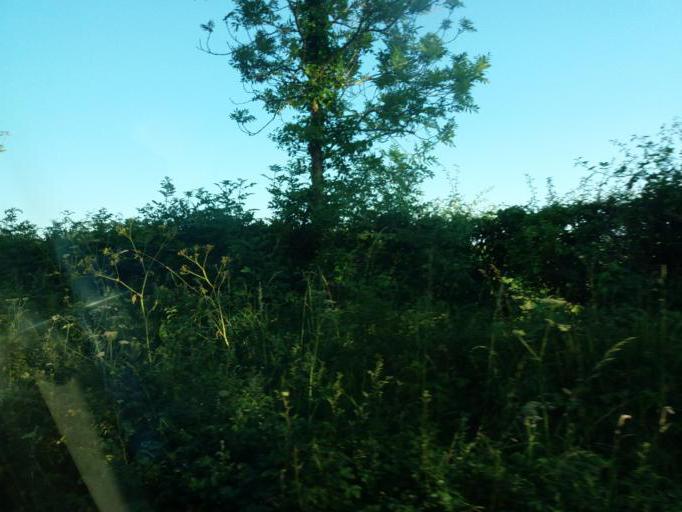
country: IE
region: Leinster
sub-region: An Mhi
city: Ashbourne
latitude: 53.5740
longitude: -6.3540
